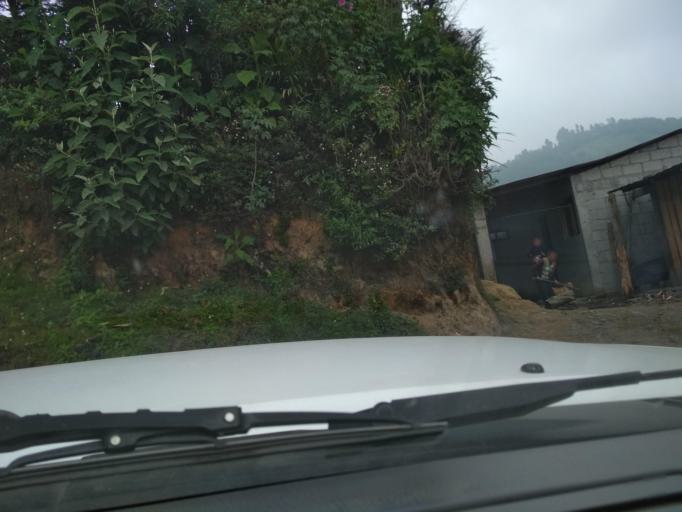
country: MX
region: Veracruz
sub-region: La Perla
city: Chilapa
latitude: 18.9893
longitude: -97.1580
